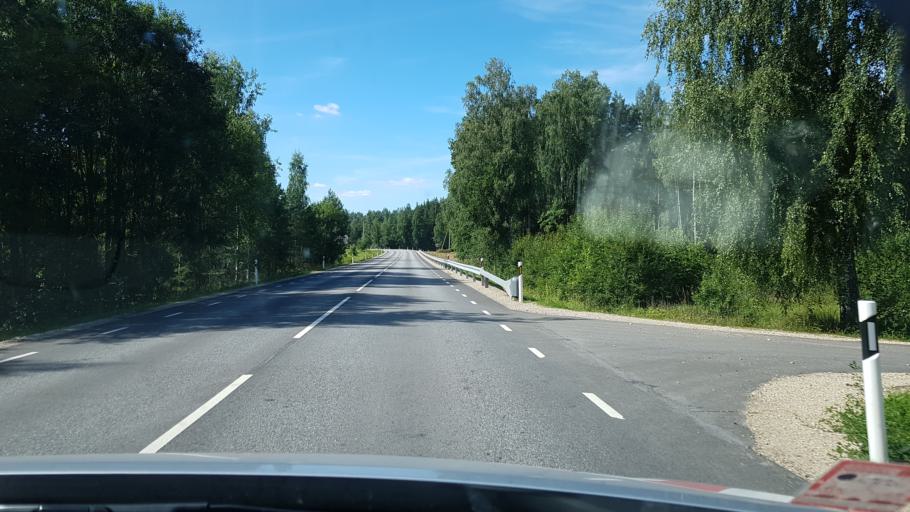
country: EE
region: Polvamaa
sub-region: Polva linn
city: Polva
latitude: 58.0391
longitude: 27.1240
